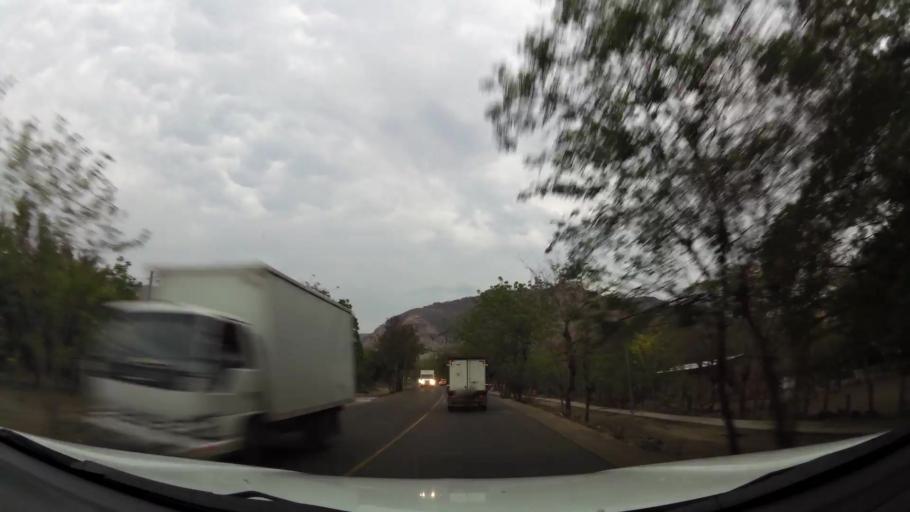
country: NI
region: Leon
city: Santa Rosa del Penon
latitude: 12.9379
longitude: -86.2081
